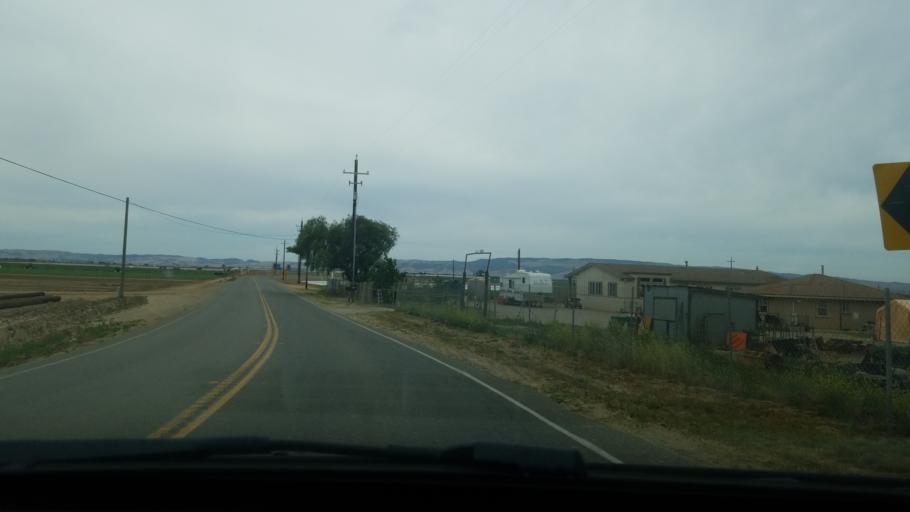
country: US
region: California
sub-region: San Luis Obispo County
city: Nipomo
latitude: 35.0097
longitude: -120.5019
